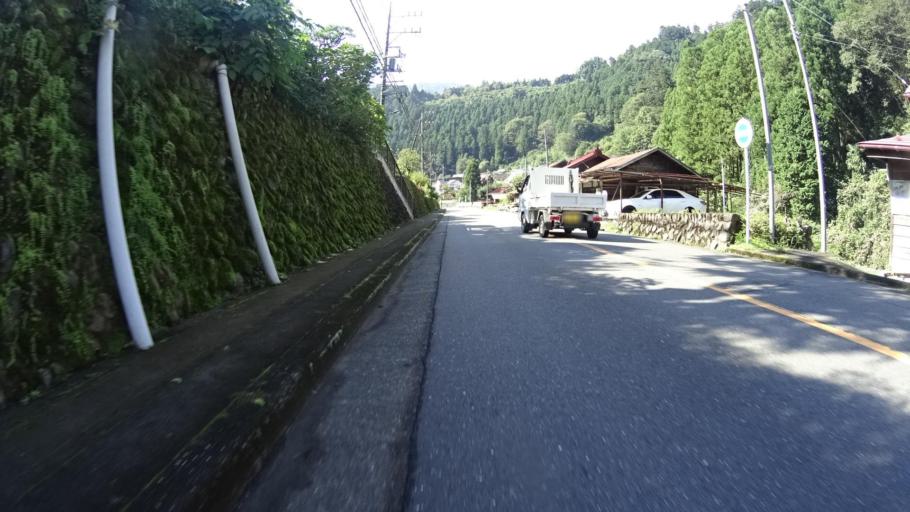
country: JP
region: Tokyo
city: Itsukaichi
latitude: 35.7397
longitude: 139.1221
